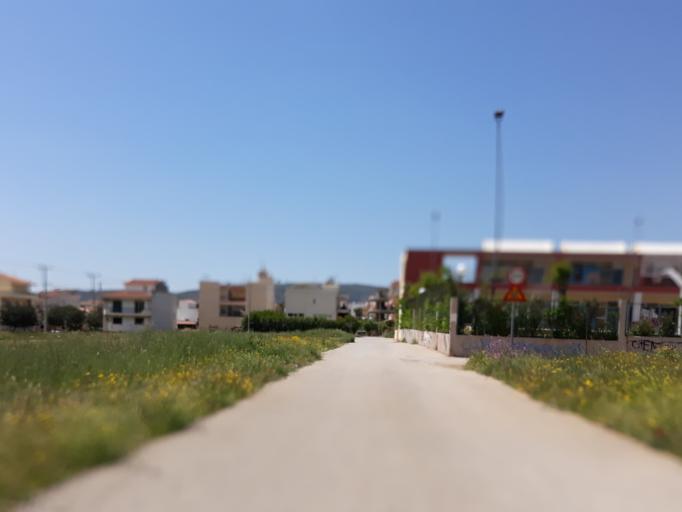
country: GR
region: Attica
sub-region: Nomarchia Dytikis Attikis
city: Ano Liosia
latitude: 38.0894
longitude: 23.7044
